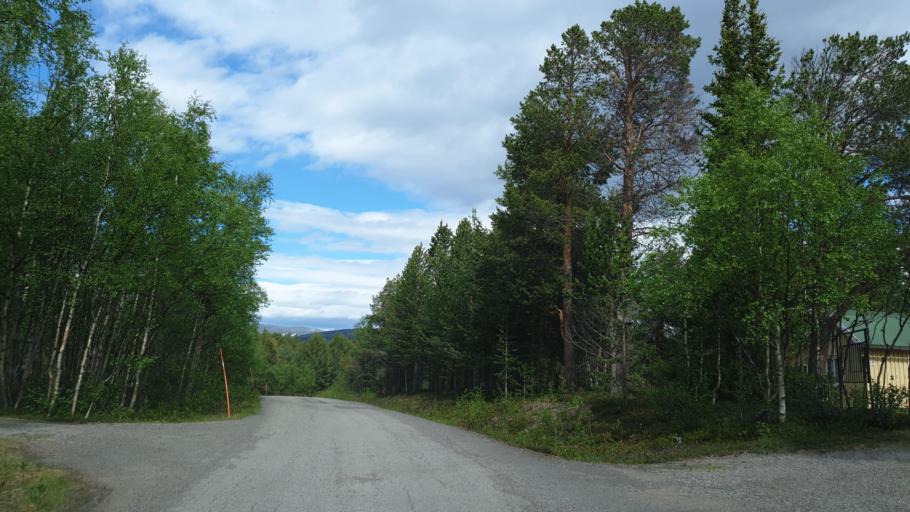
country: SE
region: Norrbotten
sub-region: Kiruna Kommun
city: Kiruna
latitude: 68.2210
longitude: 19.7134
